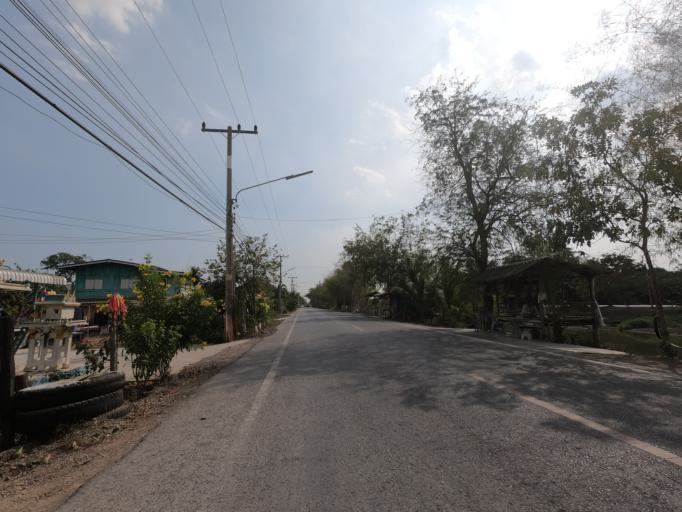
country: TH
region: Pathum Thani
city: Nong Suea
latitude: 14.1076
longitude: 100.8466
